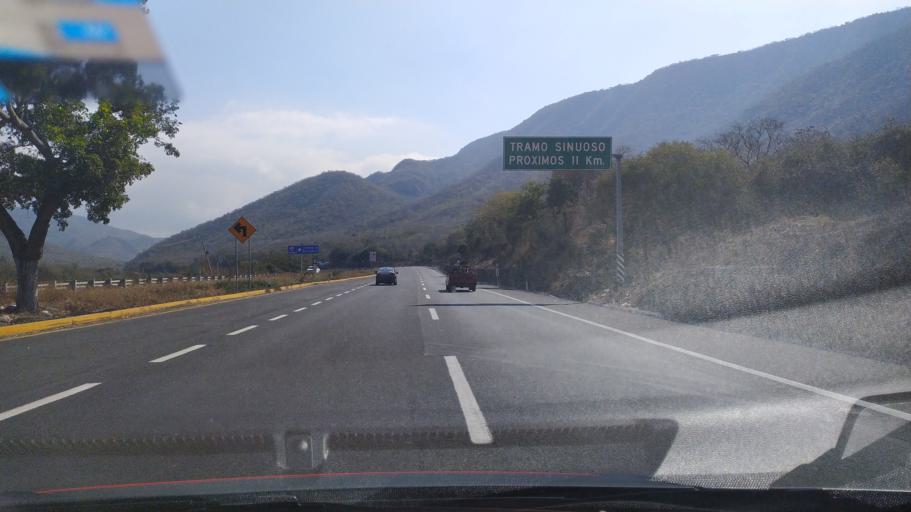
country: MX
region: Colima
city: Madrid
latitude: 19.1024
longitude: -103.7769
